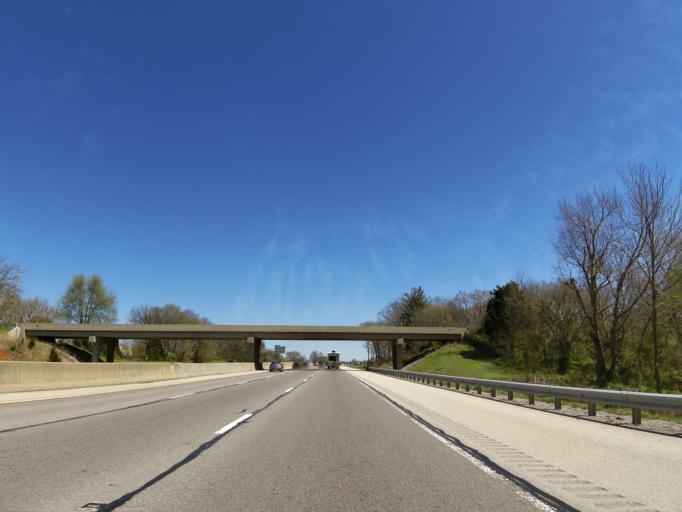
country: US
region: Kentucky
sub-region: Warren County
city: Bowling Green
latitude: 37.0095
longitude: -86.3526
